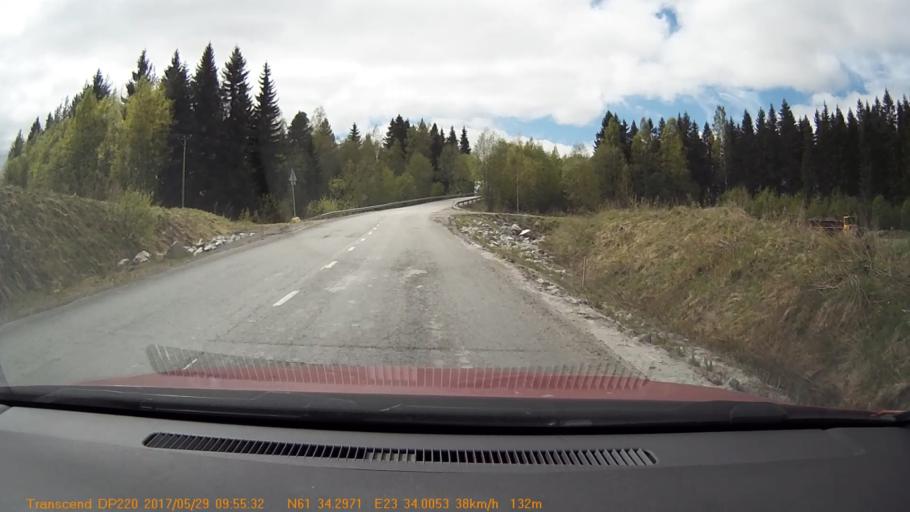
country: FI
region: Pirkanmaa
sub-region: Tampere
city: Yloejaervi
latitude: 61.5717
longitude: 23.5673
